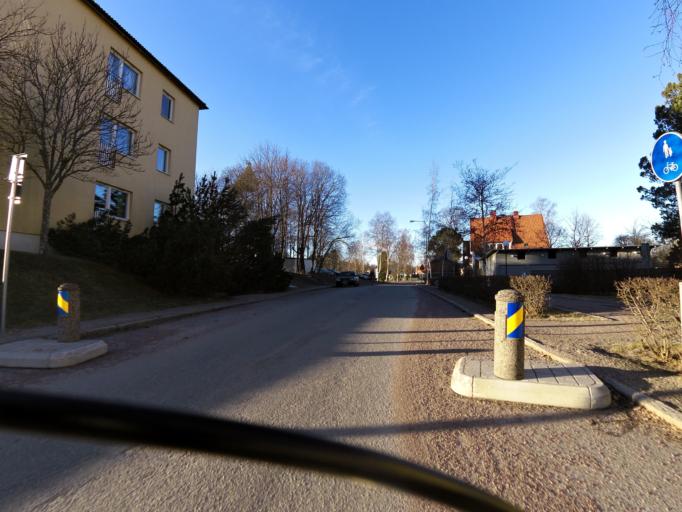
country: SE
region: Gaevleborg
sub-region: Gavle Kommun
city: Gavle
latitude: 60.6684
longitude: 17.1248
